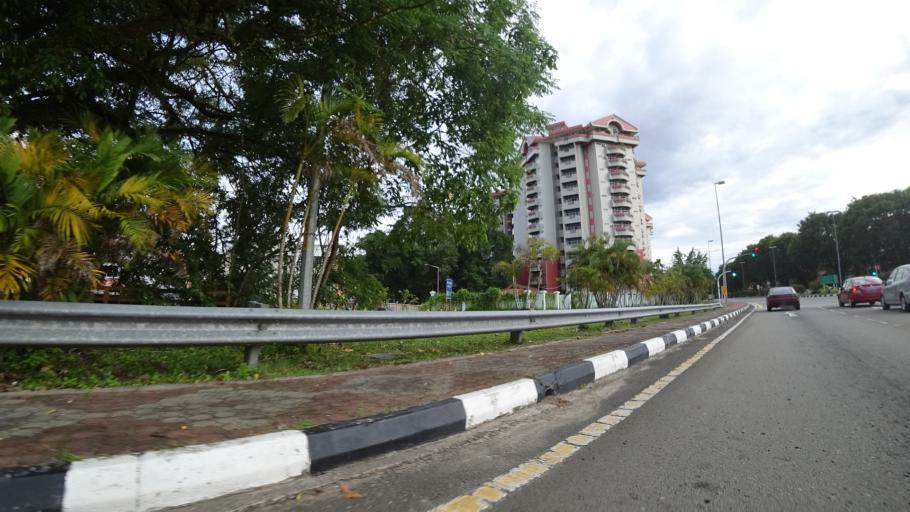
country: BN
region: Brunei and Muara
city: Bandar Seri Begawan
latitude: 4.9004
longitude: 114.9400
